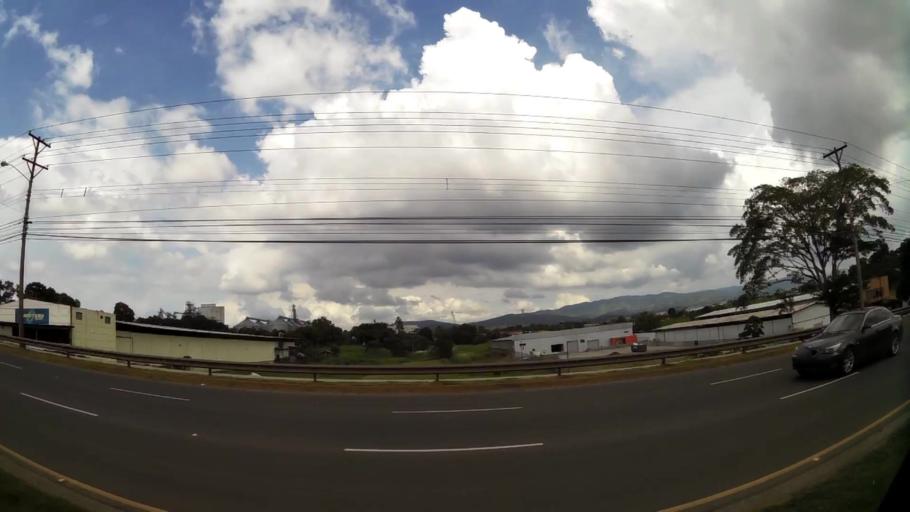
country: PA
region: Panama
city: Tocumen
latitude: 9.0669
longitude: -79.4121
